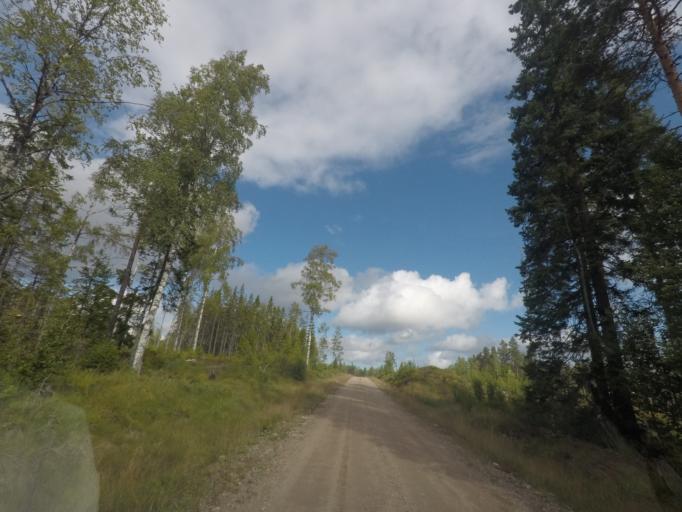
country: SE
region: Vaermland
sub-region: Filipstads Kommun
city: Lesjofors
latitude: 60.0517
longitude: 14.4419
